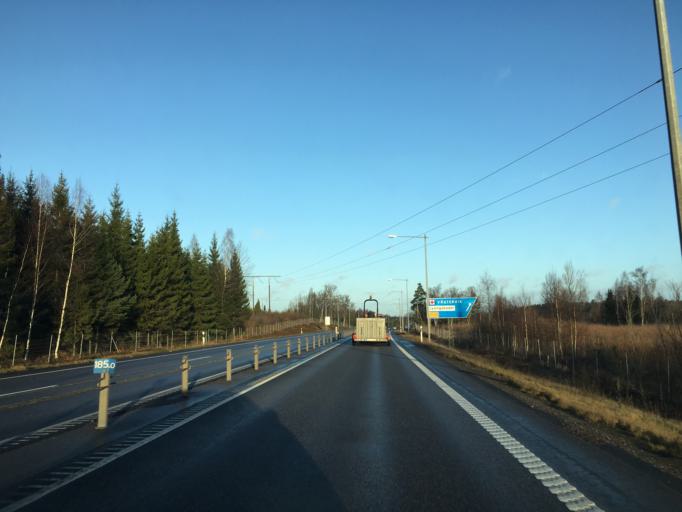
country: SE
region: Kalmar
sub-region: Vasterviks Kommun
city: Vaestervik
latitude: 57.7576
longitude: 16.5568
